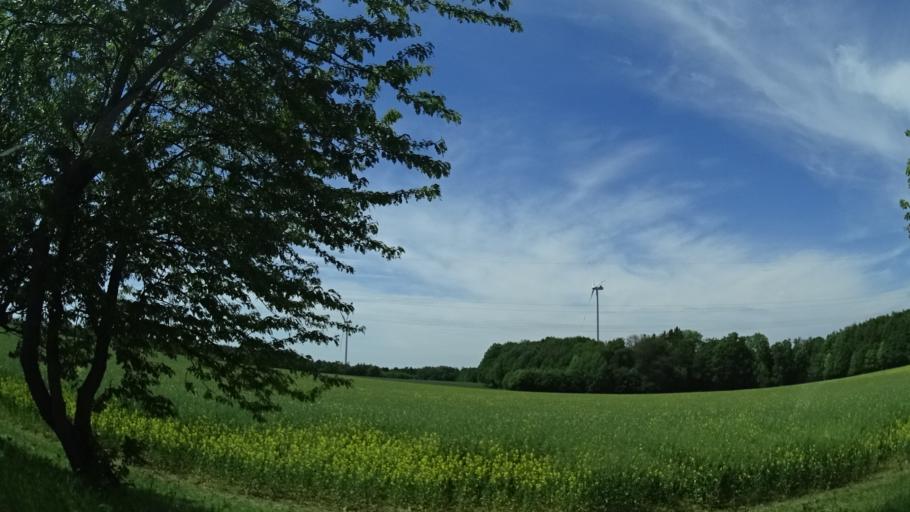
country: DE
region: Bavaria
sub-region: Regierungsbezirk Unterfranken
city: Oerlenbach
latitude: 50.1852
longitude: 10.1587
